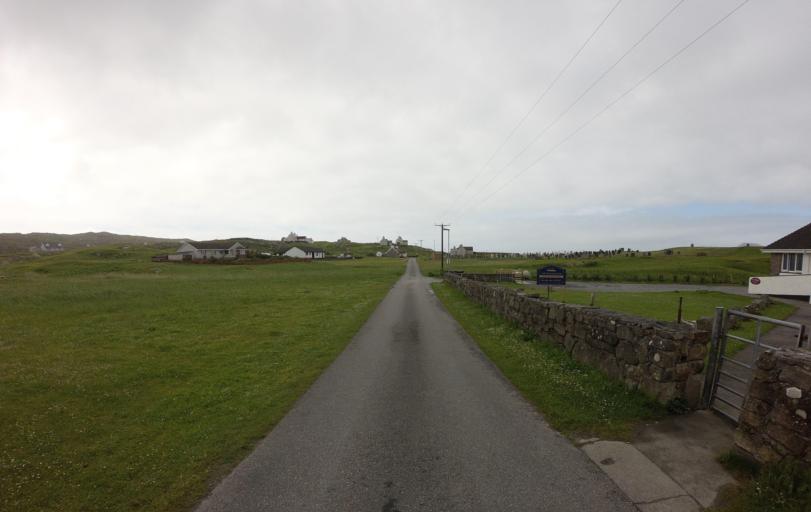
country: GB
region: Scotland
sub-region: Eilean Siar
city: Isle of South Uist
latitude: 57.0845
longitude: -7.3087
